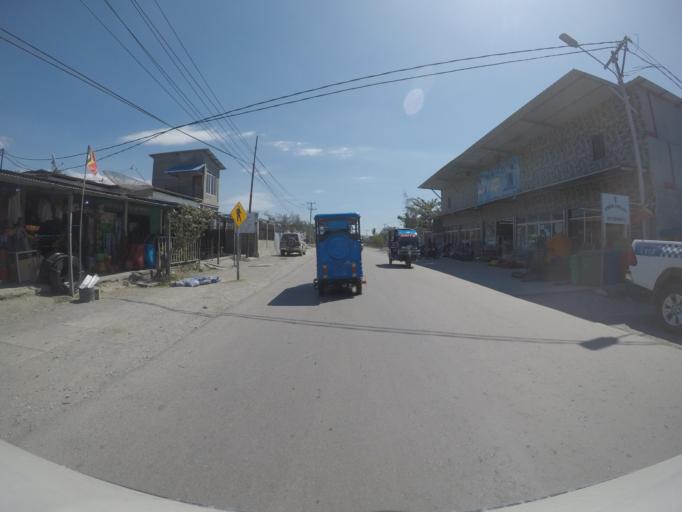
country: TL
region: Liquica
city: Liquica
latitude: -8.5907
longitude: 125.3351
